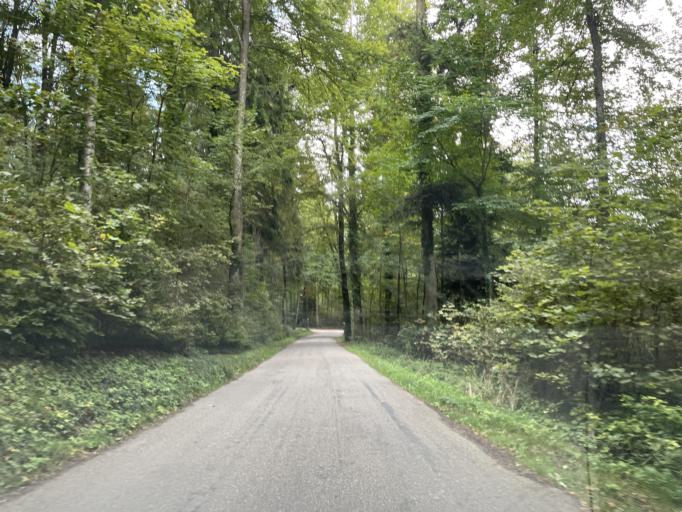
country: CH
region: Zurich
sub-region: Bezirk Winterthur
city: Seen (Kreis 3) / Waldegg
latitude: 47.4750
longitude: 8.7495
